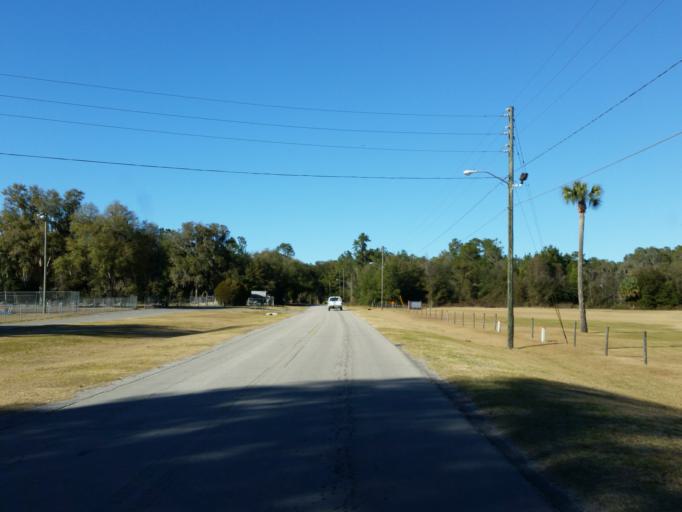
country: US
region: Florida
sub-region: Hamilton County
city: Jasper
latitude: 30.5082
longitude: -82.9527
